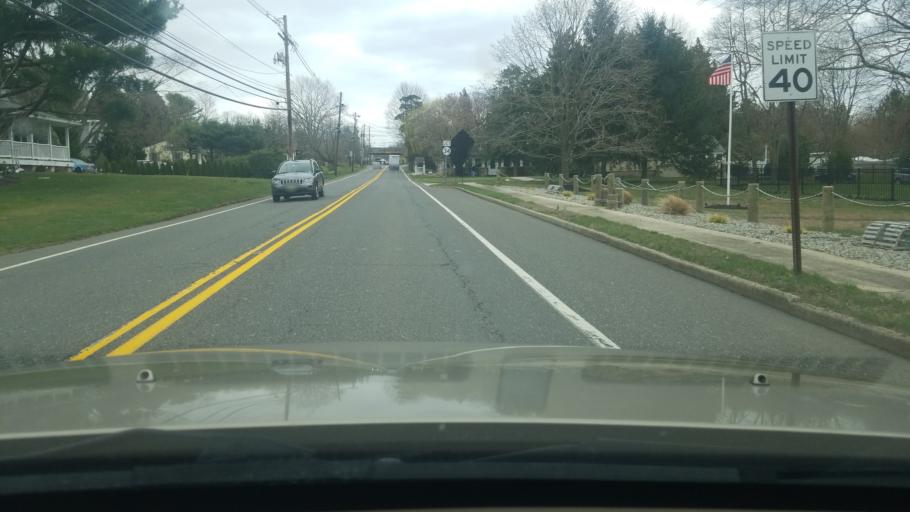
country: US
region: New Jersey
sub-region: Monmouth County
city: Manasquan
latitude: 40.1414
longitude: -74.0959
